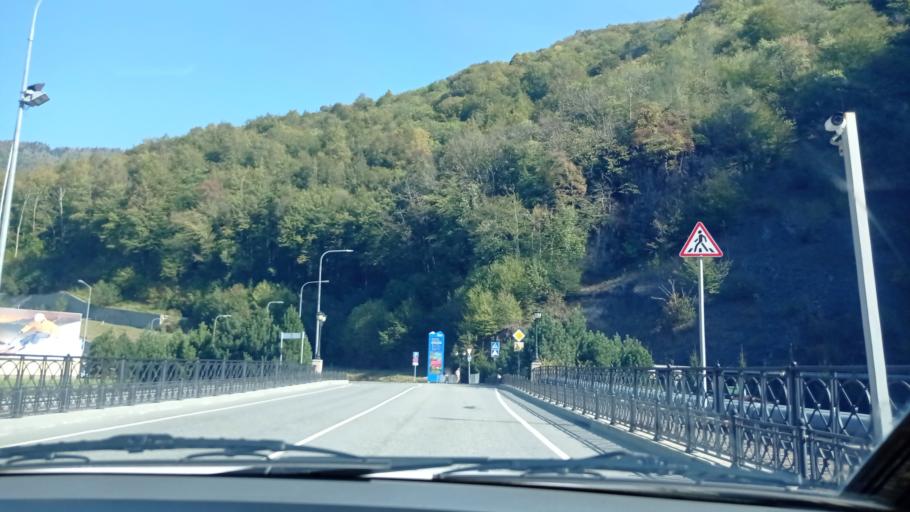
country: RU
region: Krasnodarskiy
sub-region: Sochi City
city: Krasnaya Polyana
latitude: 43.6822
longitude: 40.2786
